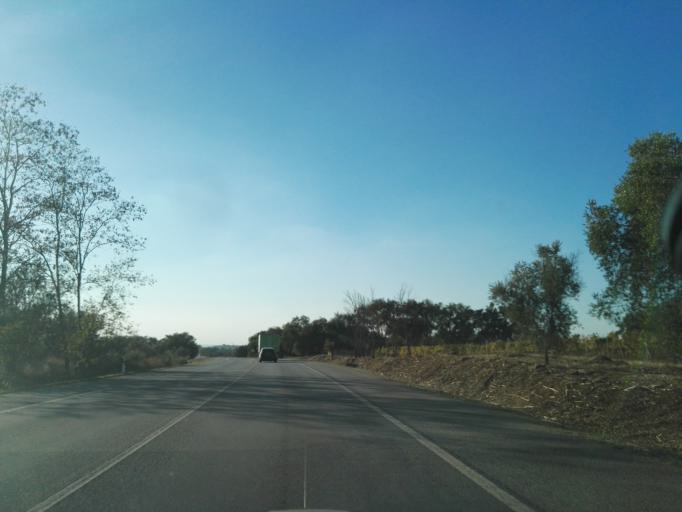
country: PT
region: Evora
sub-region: Estremoz
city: Estremoz
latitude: 38.8323
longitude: -7.5406
